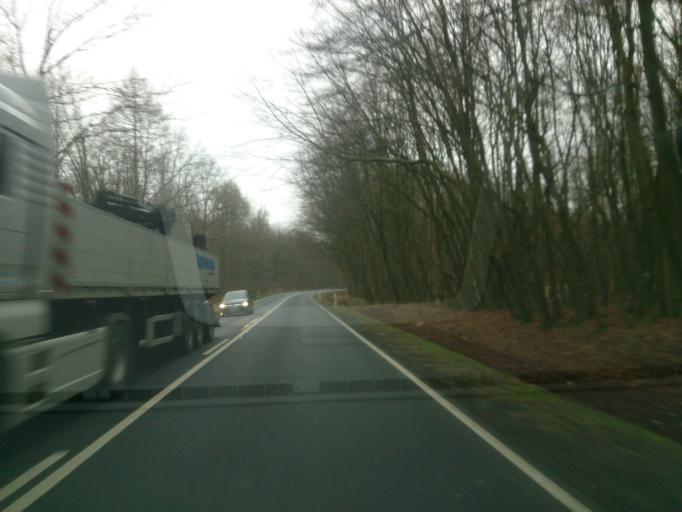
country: DE
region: Mecklenburg-Vorpommern
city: Borrentin
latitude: 53.7548
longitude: 12.9324
